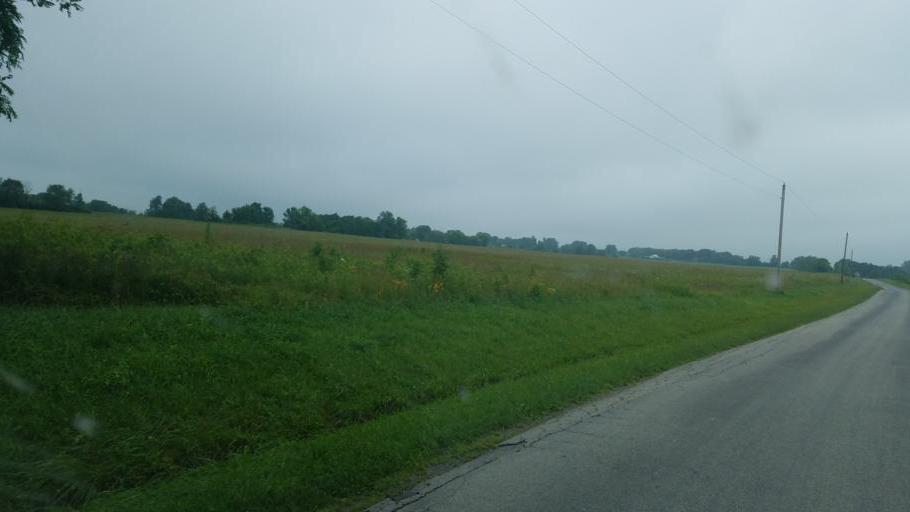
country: US
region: Ohio
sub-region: Highland County
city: Hillsboro
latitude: 39.2458
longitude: -83.5454
